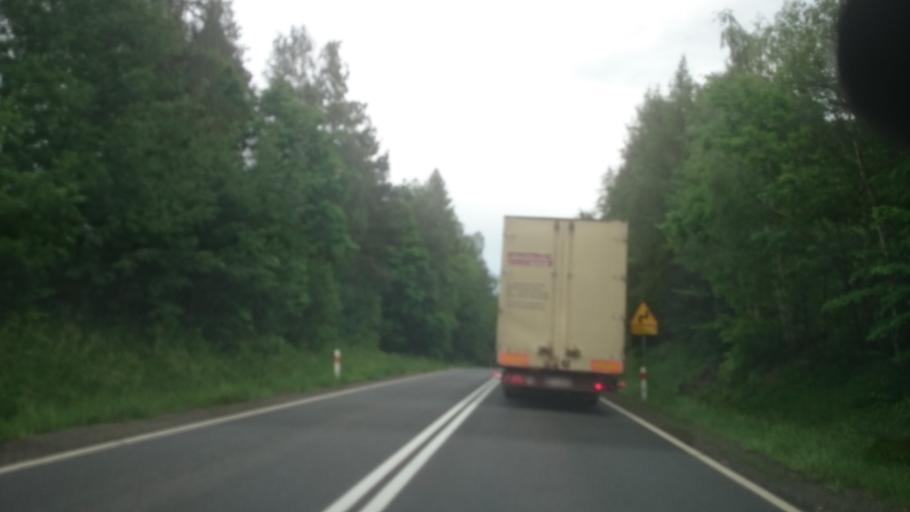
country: PL
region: Lower Silesian Voivodeship
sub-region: Powiat klodzki
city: Klodzko
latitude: 50.4332
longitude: 16.7109
